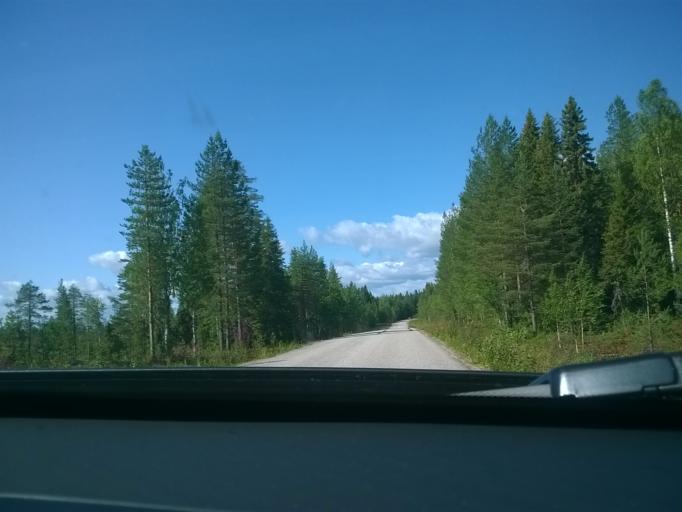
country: FI
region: Kainuu
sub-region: Kehys-Kainuu
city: Kuhmo
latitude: 64.4605
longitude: 29.6120
